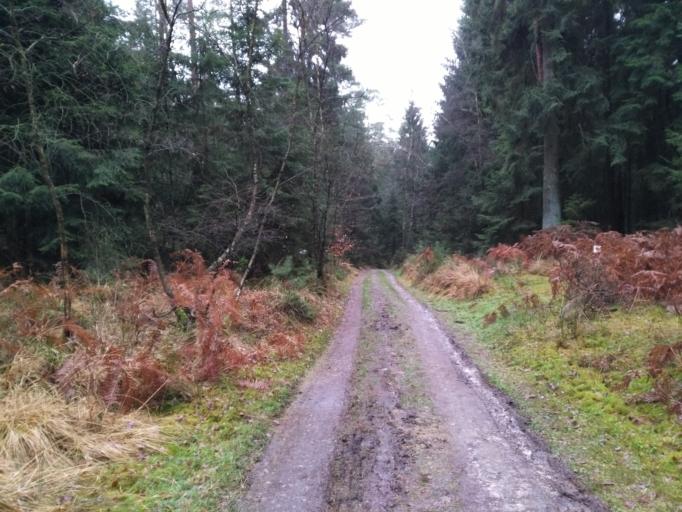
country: DE
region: Lower Saxony
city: Neu Wulmstorf
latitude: 53.4392
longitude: 9.8578
